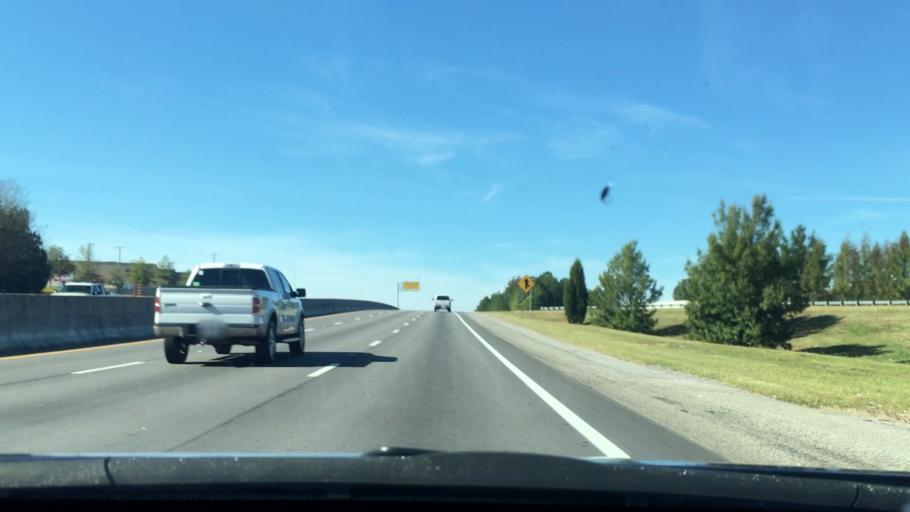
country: US
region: South Carolina
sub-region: Lexington County
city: Irmo
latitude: 34.0916
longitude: -81.1664
